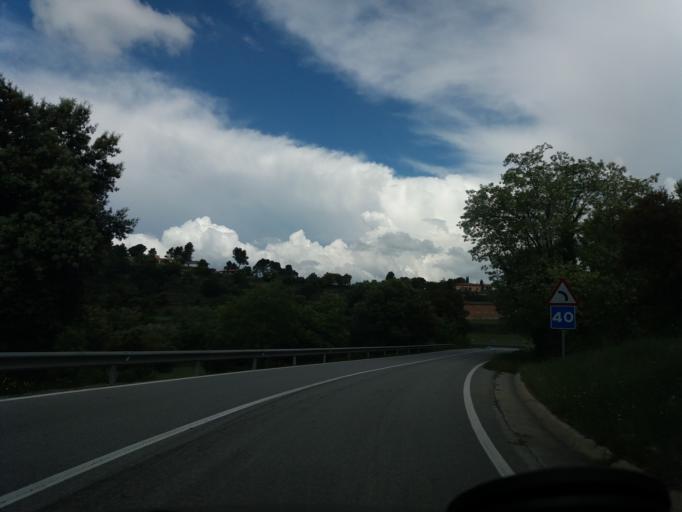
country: ES
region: Catalonia
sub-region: Provincia de Barcelona
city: Artes
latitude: 41.7864
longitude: 1.9887
